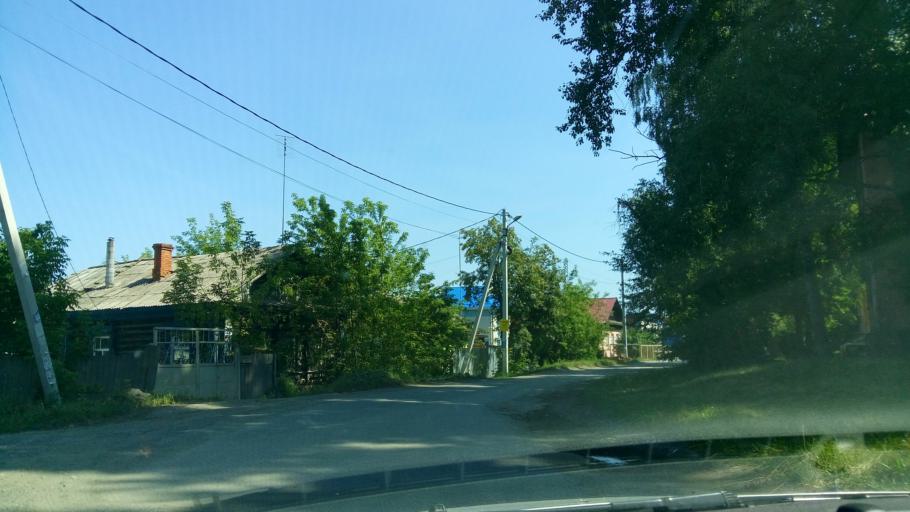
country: RU
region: Sverdlovsk
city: Yekaterinburg
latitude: 56.8773
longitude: 60.6834
